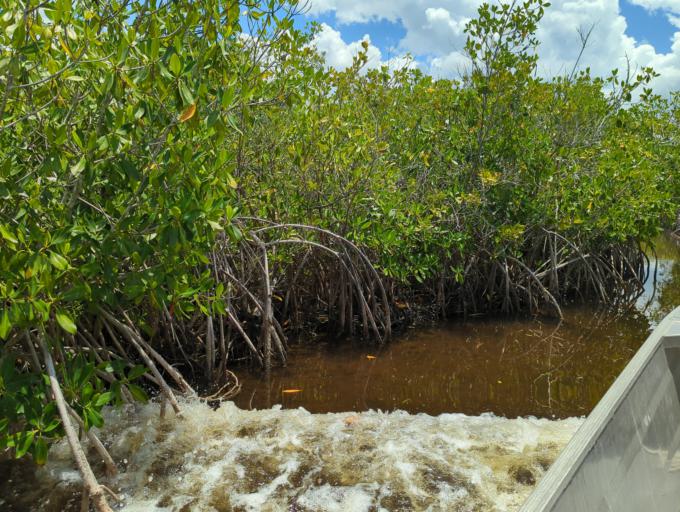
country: US
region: Florida
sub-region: Collier County
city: Marco
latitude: 25.9025
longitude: -81.3746
